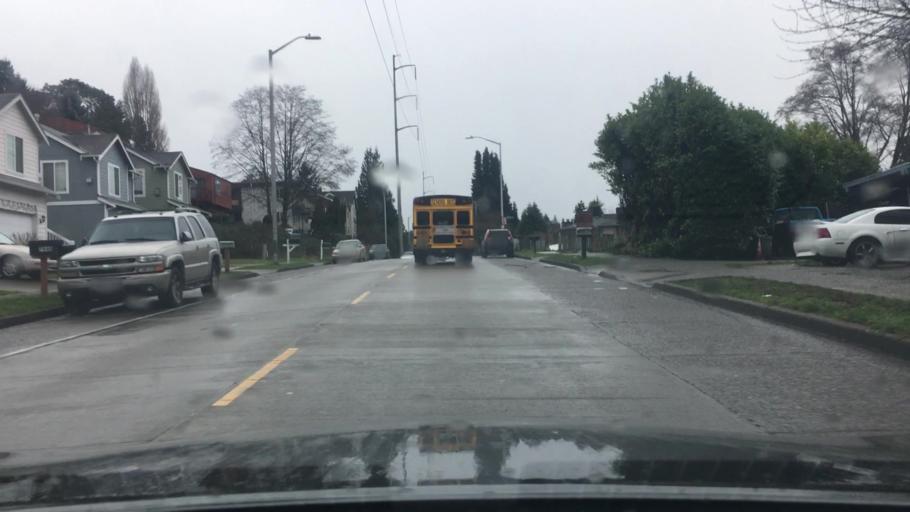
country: US
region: Washington
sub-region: King County
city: White Center
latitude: 47.5307
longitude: -122.3605
